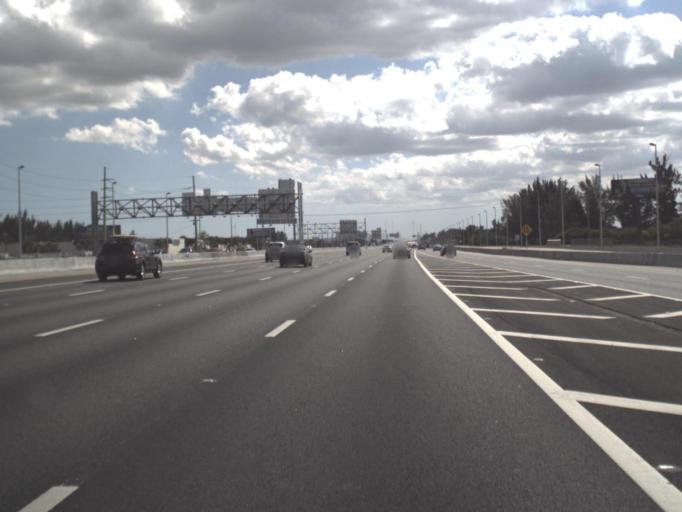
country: US
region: Florida
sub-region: Broward County
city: Broadview Park
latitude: 26.0800
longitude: -80.2162
